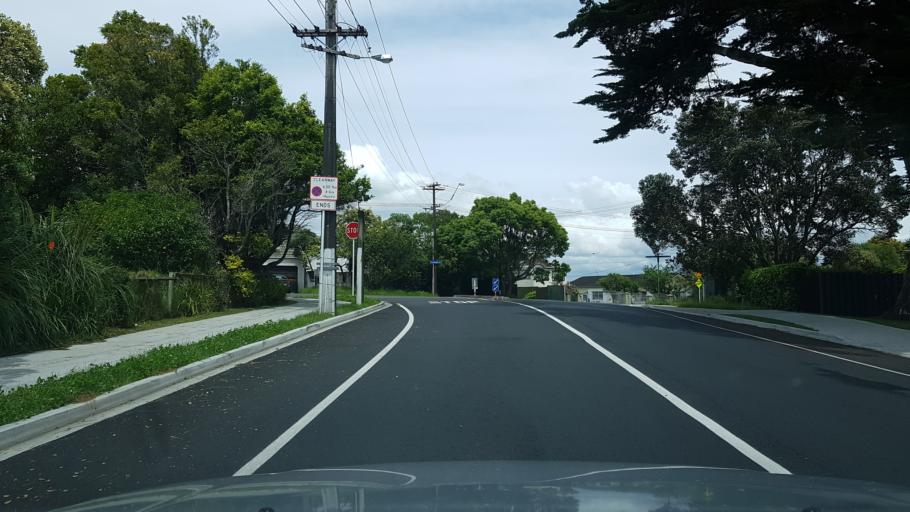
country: NZ
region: Auckland
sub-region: Auckland
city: North Shore
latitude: -36.8027
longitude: 174.7459
